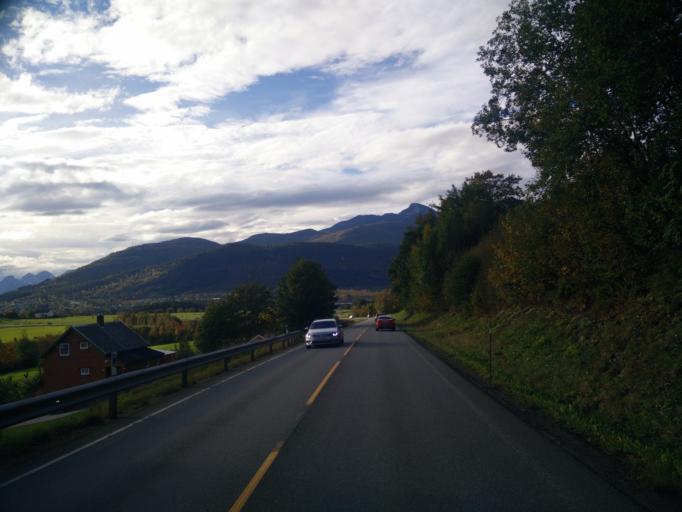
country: NO
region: More og Romsdal
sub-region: Vestnes
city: Vestnes
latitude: 62.6344
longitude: 7.0755
